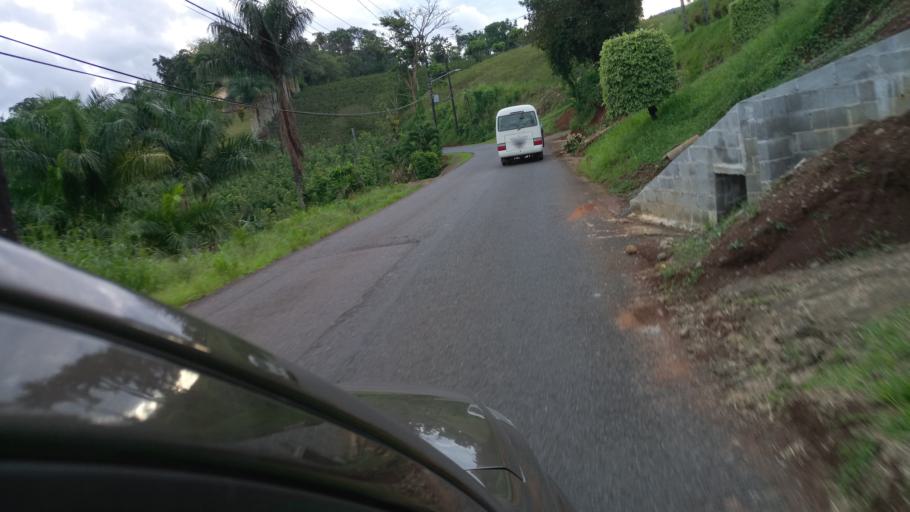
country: CR
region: Alajuela
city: Pocosol
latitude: 10.3340
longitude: -84.5816
